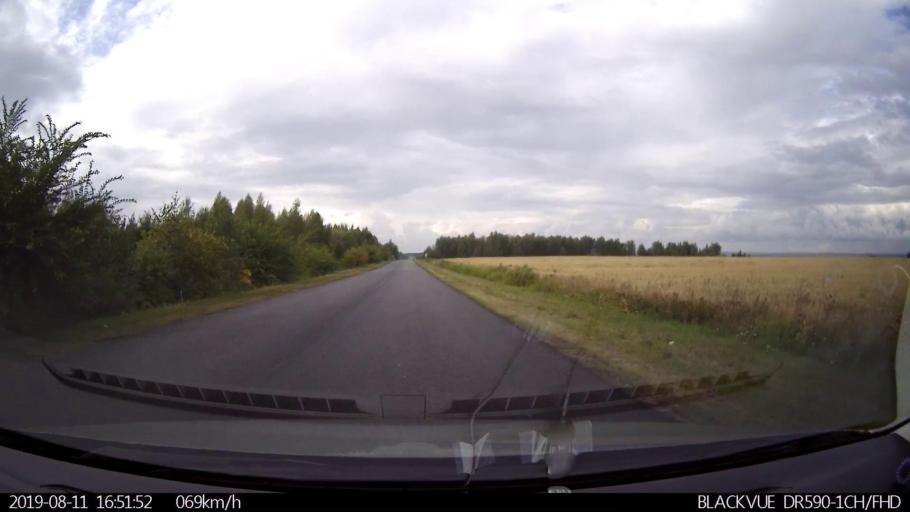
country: RU
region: Ulyanovsk
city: Mayna
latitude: 54.2416
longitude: 47.6758
